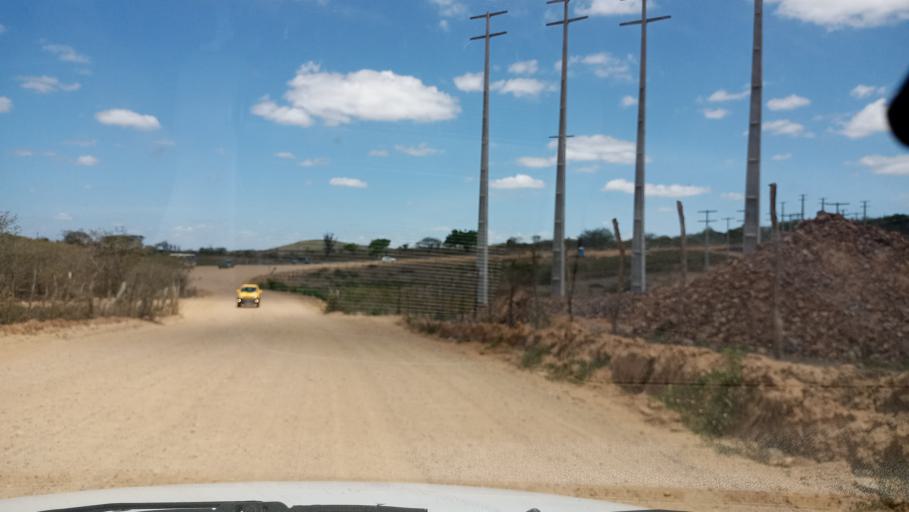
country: BR
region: Rio Grande do Norte
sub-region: Sao Paulo Do Potengi
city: Sao Paulo do Potengi
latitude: -5.7887
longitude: -35.9164
